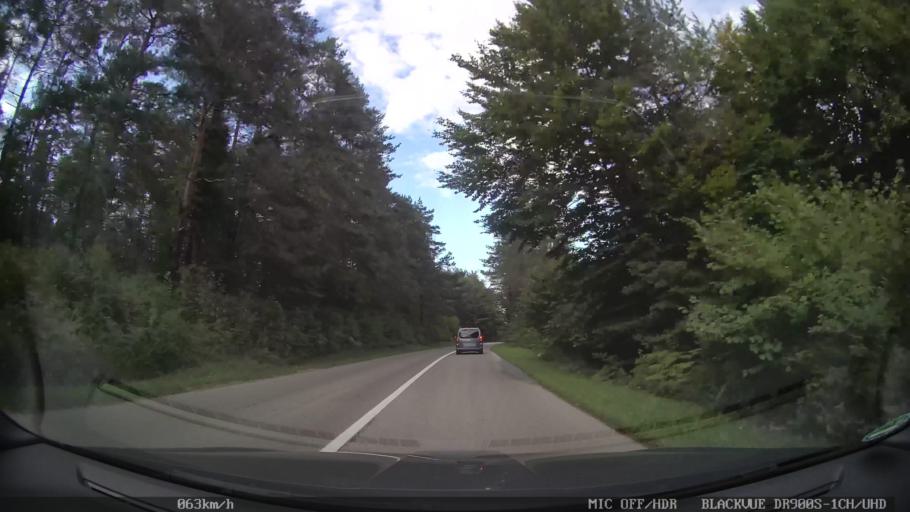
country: HR
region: Karlovacka
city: Plaski
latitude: 45.0431
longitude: 15.4161
